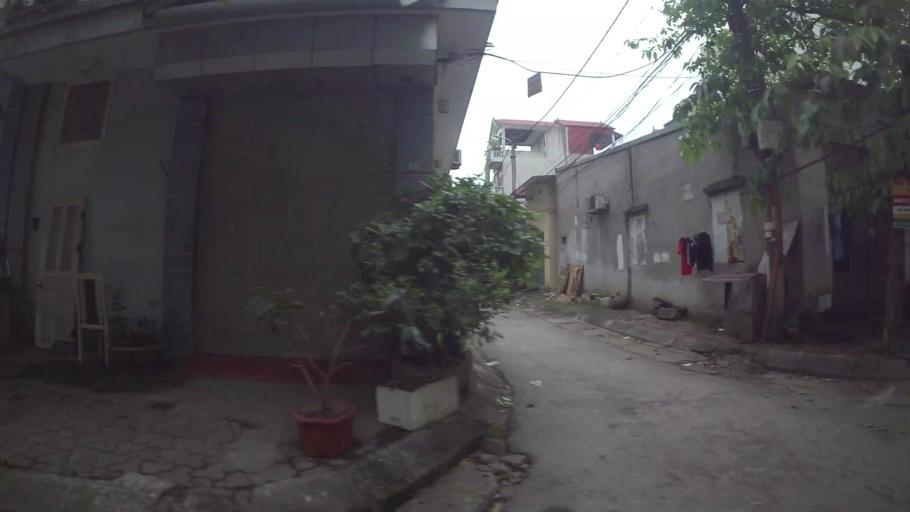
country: VN
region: Ha Noi
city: Van Dien
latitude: 20.9763
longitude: 105.8829
